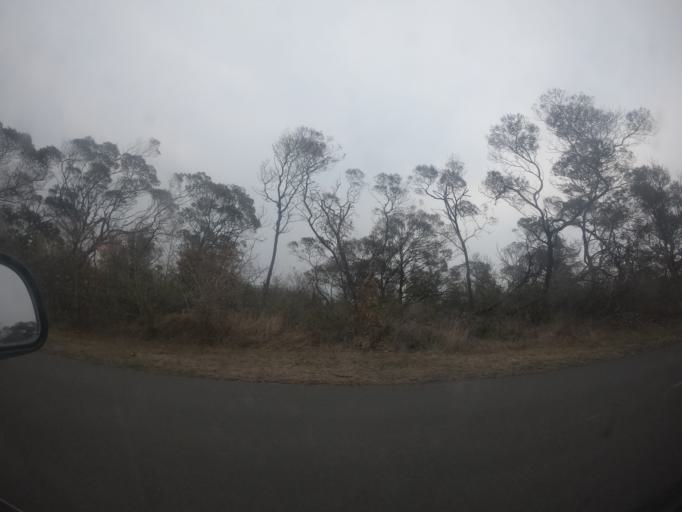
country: AU
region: New South Wales
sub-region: Shellharbour
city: Croom
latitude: -34.6131
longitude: 150.8538
